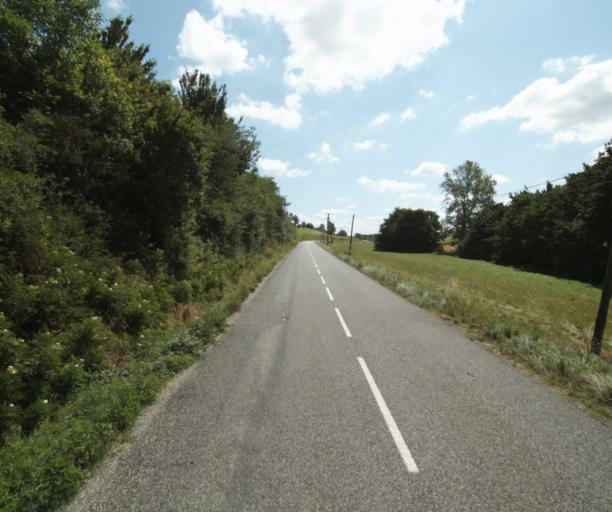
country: FR
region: Midi-Pyrenees
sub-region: Departement de la Haute-Garonne
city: Auriac-sur-Vendinelle
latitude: 43.4805
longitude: 1.7979
